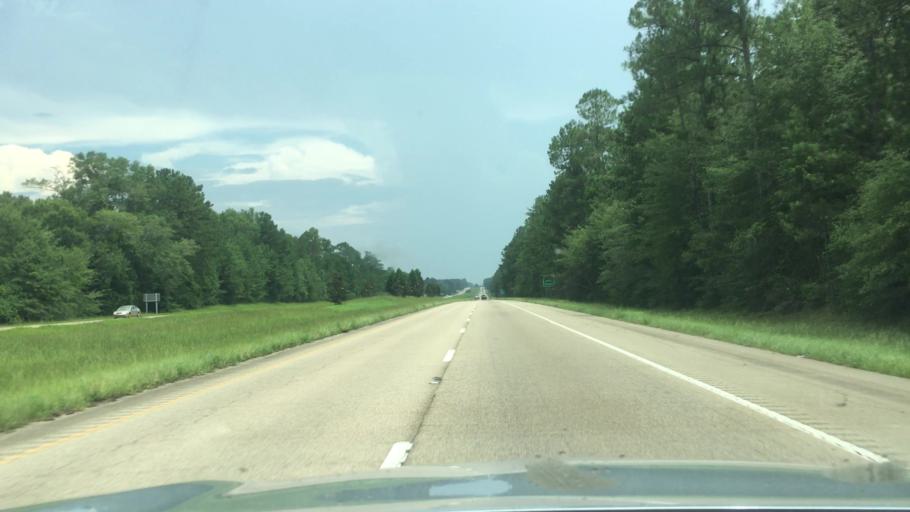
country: US
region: Mississippi
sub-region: Lamar County
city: Lumberton
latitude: 30.9815
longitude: -89.4283
